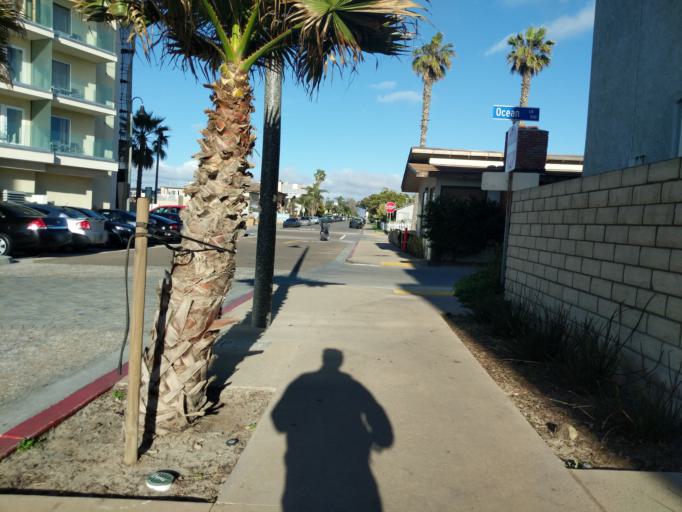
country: US
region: California
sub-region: San Diego County
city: Imperial Beach
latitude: 32.5811
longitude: -117.1324
